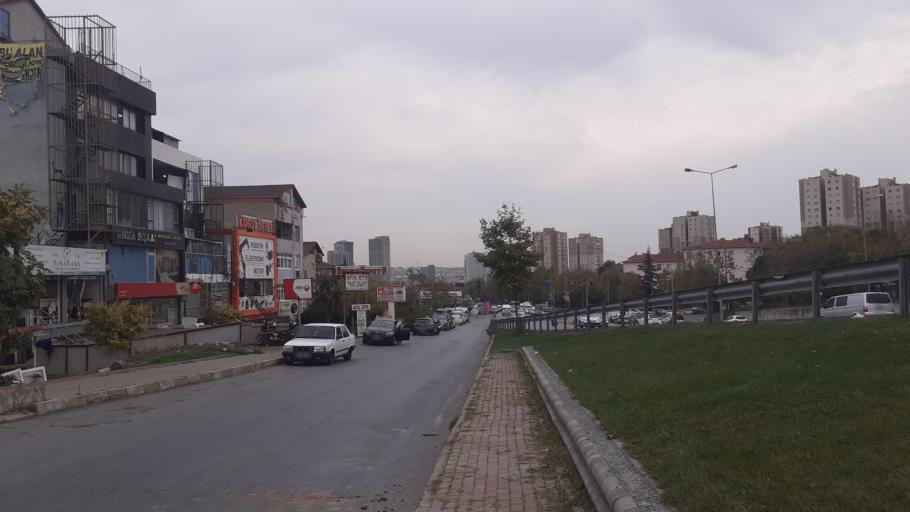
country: TR
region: Istanbul
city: Mahmutbey
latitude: 41.0497
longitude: 28.7965
